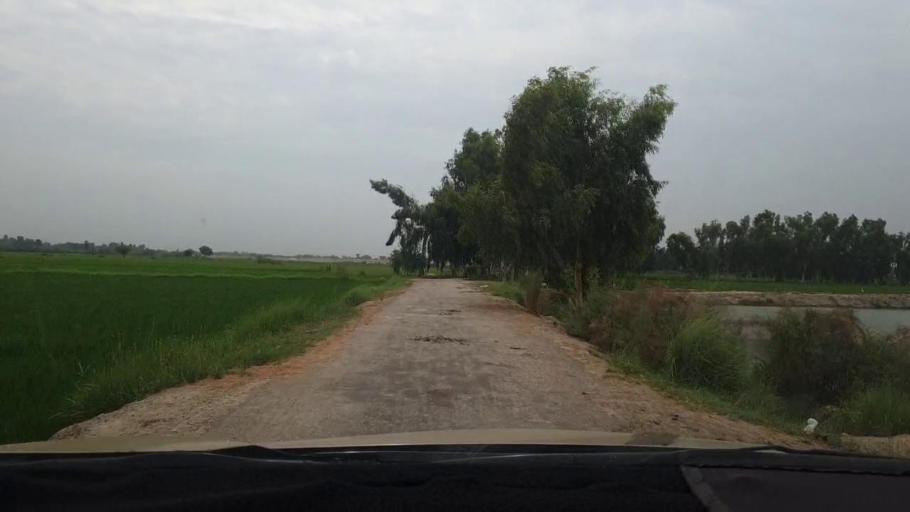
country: PK
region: Sindh
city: Naudero
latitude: 27.6228
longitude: 68.3265
